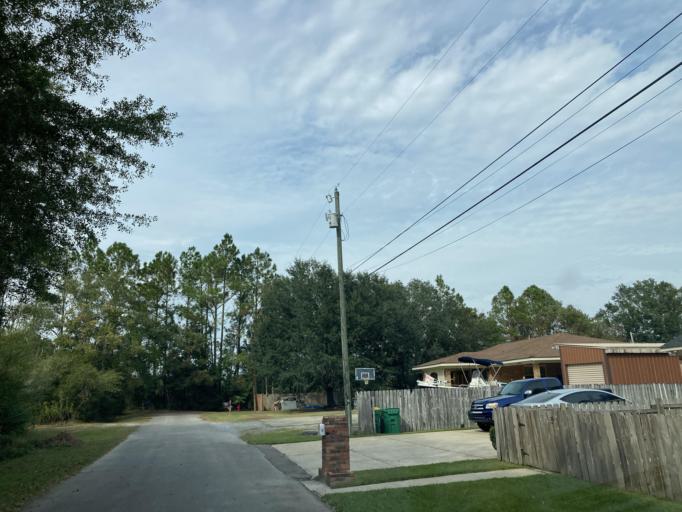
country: US
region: Mississippi
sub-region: Jackson County
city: Saint Martin
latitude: 30.4790
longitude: -88.8452
